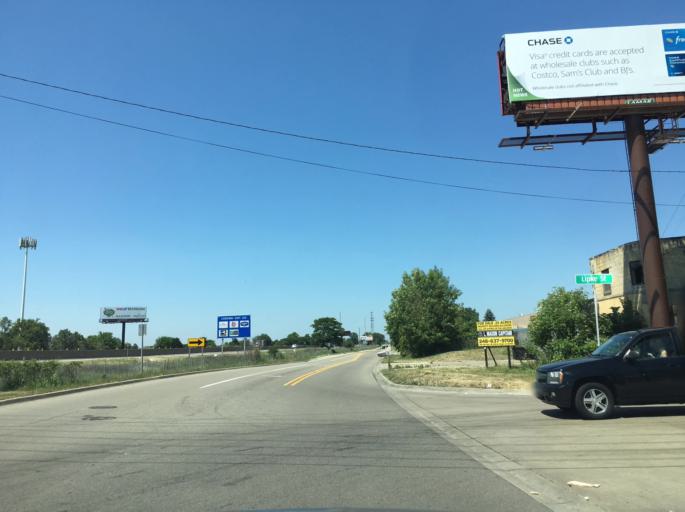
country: US
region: Michigan
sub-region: Macomb County
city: Saint Clair Shores
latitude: 42.5402
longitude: -82.8895
